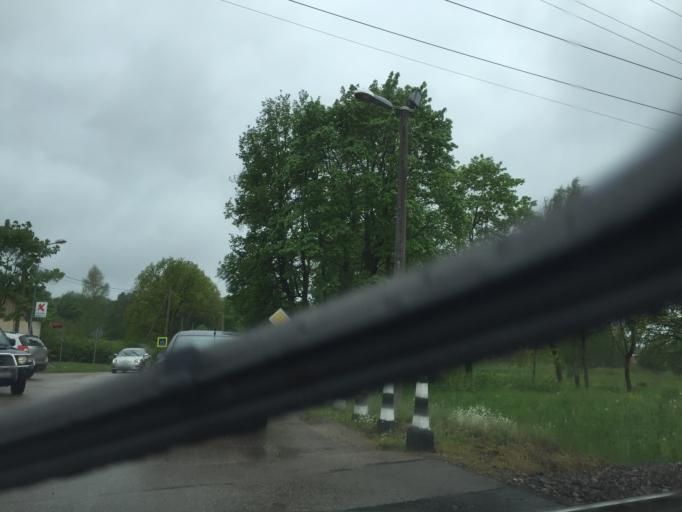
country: LV
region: Lielvarde
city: Lielvarde
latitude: 56.7225
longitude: 24.8052
